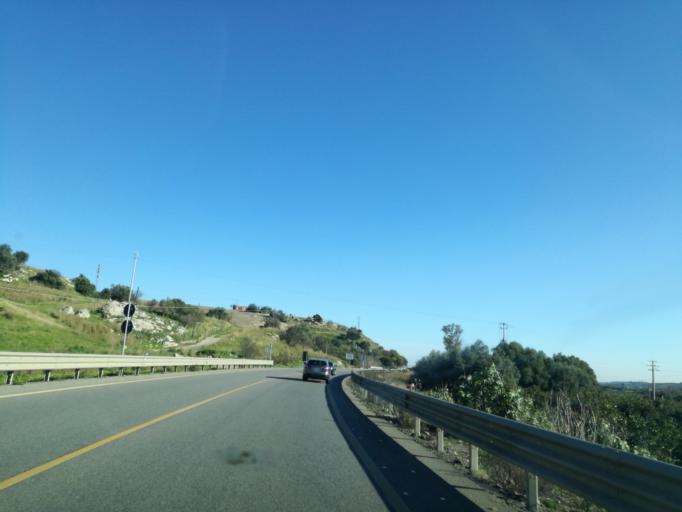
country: IT
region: Sicily
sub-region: Catania
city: Ramacca
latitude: 37.3631
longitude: 14.7146
